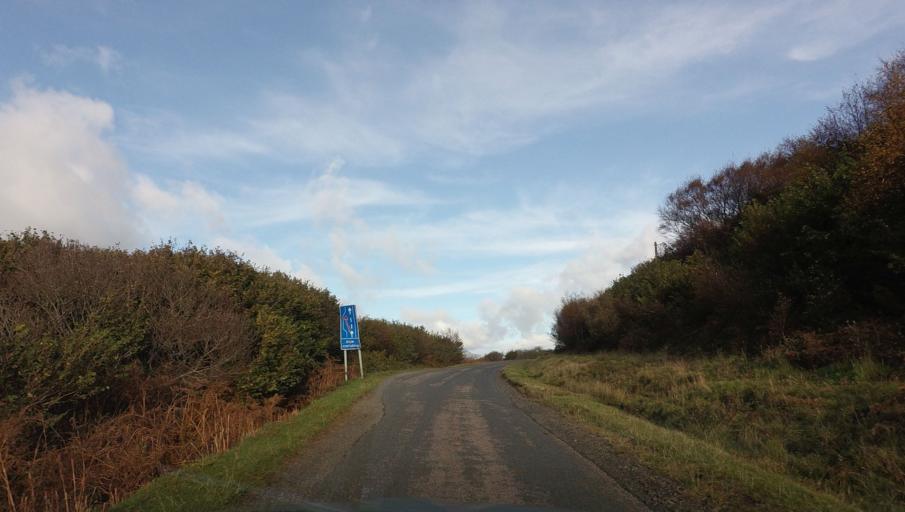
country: GB
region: Scotland
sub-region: Argyll and Bute
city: Isle Of Mull
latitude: 56.3296
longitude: -6.1970
